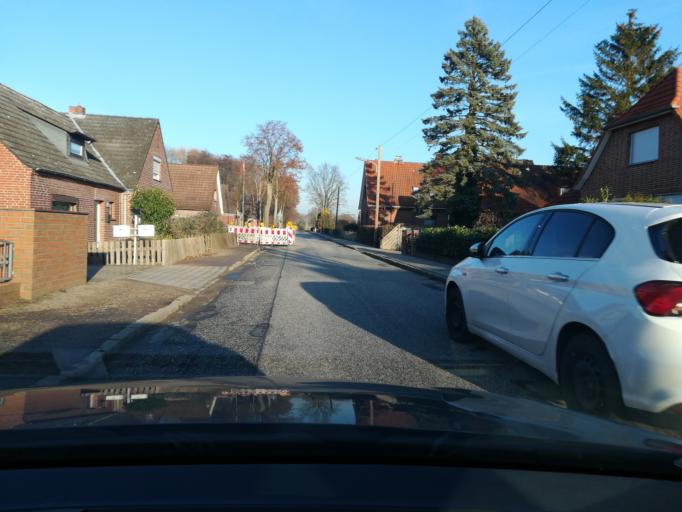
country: DE
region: Lower Saxony
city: Stelle
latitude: 53.4532
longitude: 10.1375
